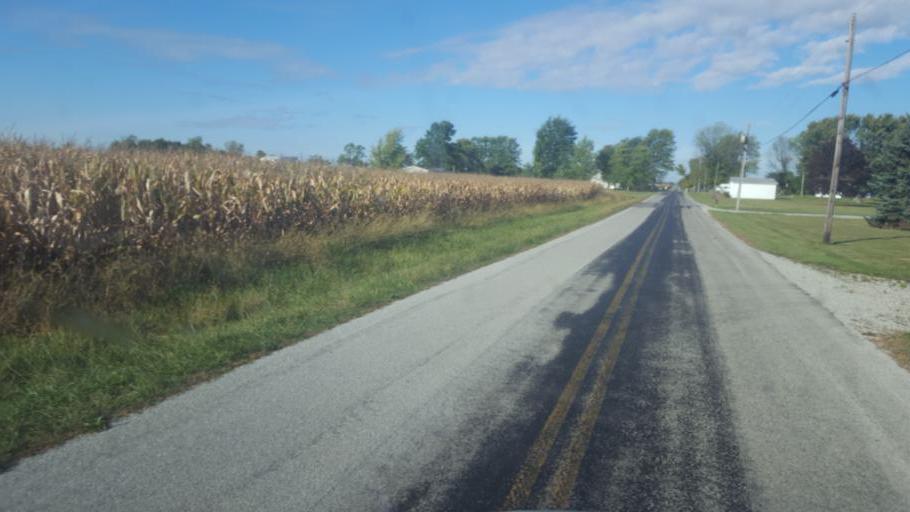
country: US
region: Ohio
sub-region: Crawford County
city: Bucyrus
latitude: 40.6888
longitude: -83.0053
